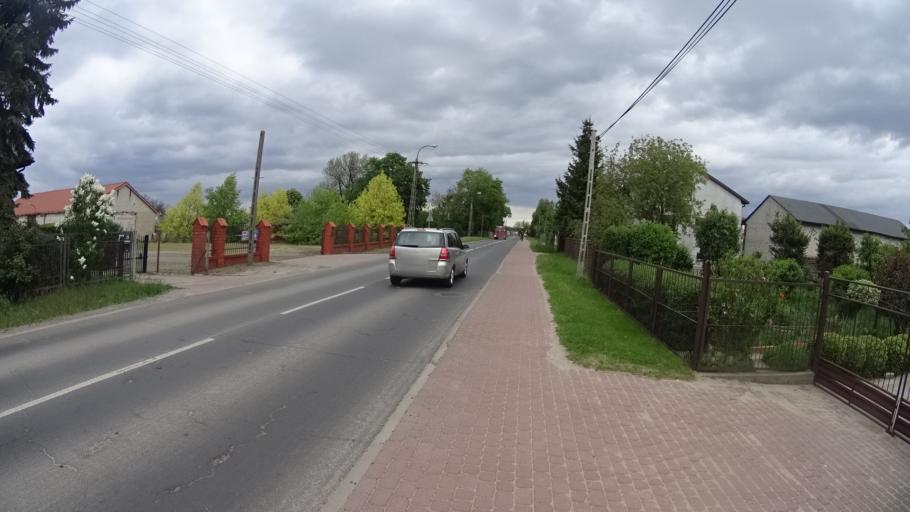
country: PL
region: Masovian Voivodeship
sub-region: Powiat warszawski zachodni
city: Babice
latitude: 52.2427
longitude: 20.8473
